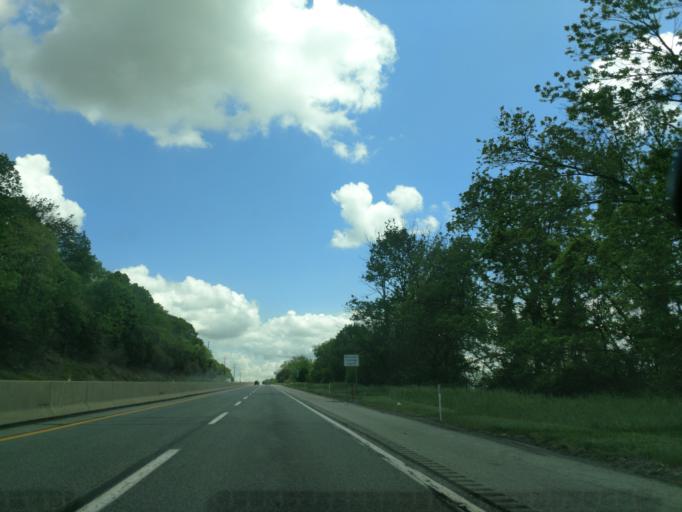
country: US
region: Pennsylvania
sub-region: Lancaster County
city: Denver
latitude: 40.2308
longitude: -76.1238
